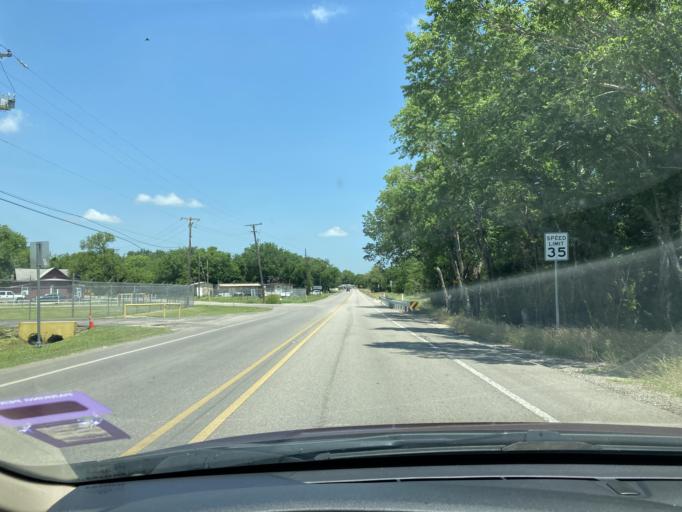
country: US
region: Texas
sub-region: Navarro County
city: Corsicana
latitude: 32.0777
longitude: -96.4632
